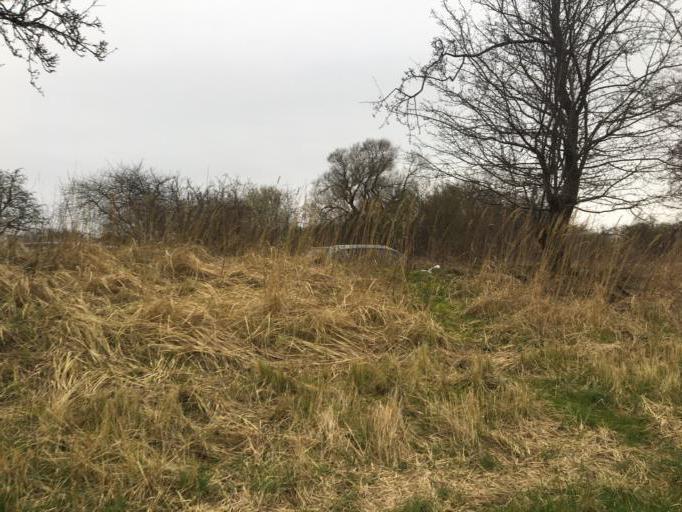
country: DK
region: Capital Region
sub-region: Ballerup Kommune
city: Ballerup
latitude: 55.6986
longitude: 12.3593
